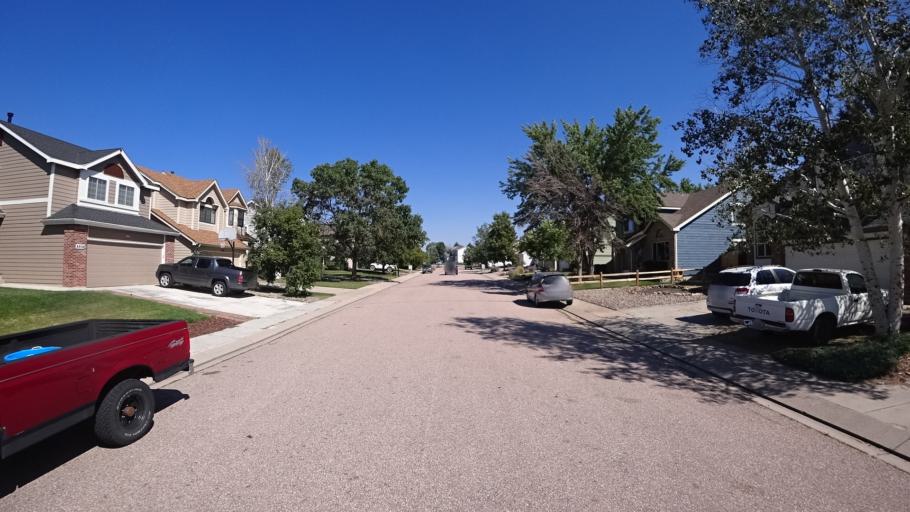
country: US
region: Colorado
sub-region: El Paso County
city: Black Forest
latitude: 38.9584
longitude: -104.7517
